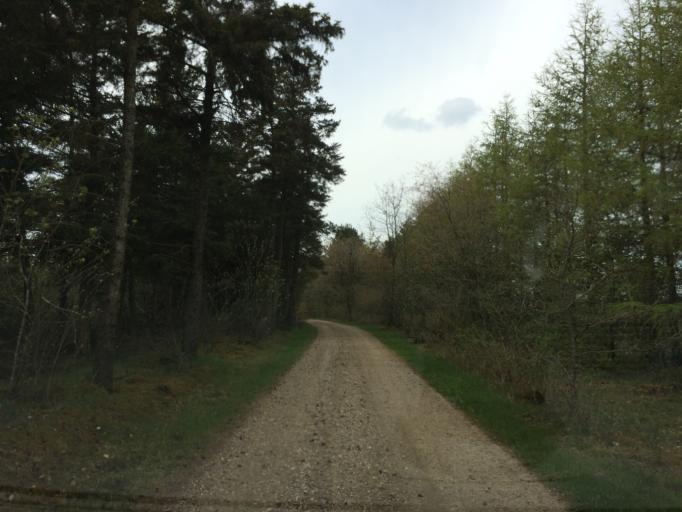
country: DK
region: Central Jutland
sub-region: Holstebro Kommune
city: Ulfborg
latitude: 56.2187
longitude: 8.4803
